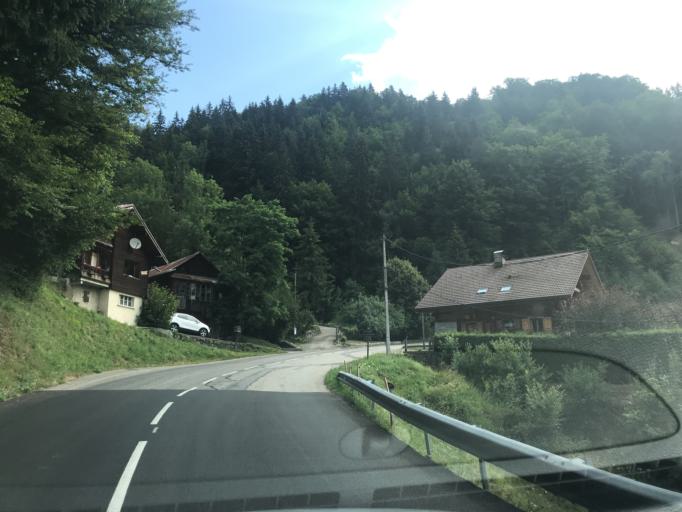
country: FR
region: Rhone-Alpes
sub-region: Departement de la Haute-Savoie
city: Thones
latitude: 45.8610
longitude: 6.3459
